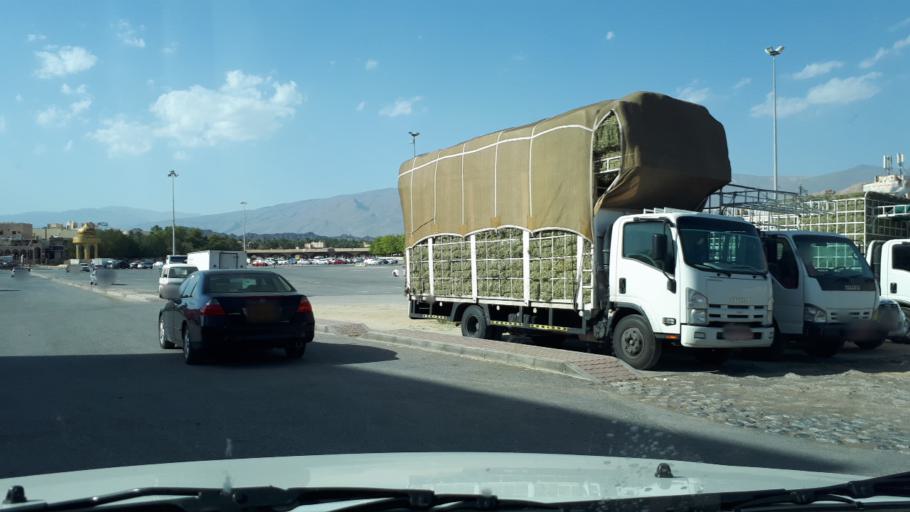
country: OM
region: Muhafazat ad Dakhiliyah
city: Nizwa
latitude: 22.9311
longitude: 57.5331
